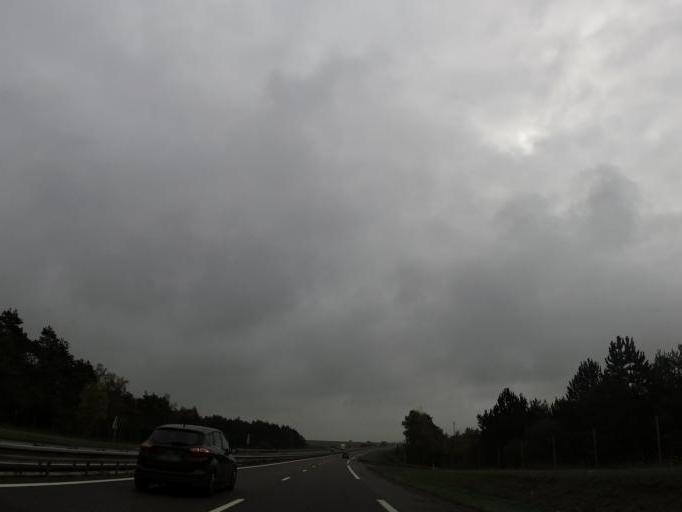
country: FR
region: Champagne-Ardenne
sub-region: Departement de la Marne
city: Fagnieres
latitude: 49.0394
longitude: 4.3443
